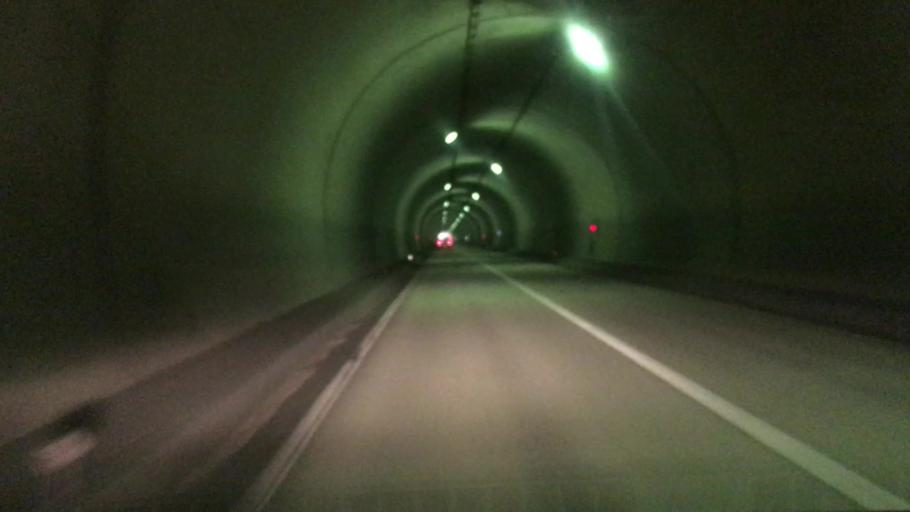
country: JP
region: Hyogo
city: Toyooka
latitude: 35.4193
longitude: 134.7409
